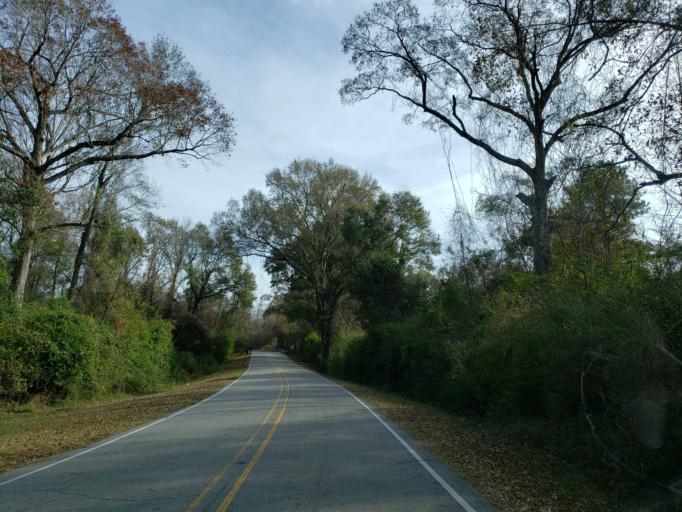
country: US
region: Mississippi
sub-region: Forrest County
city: Rawls Springs
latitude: 31.3885
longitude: -89.3790
